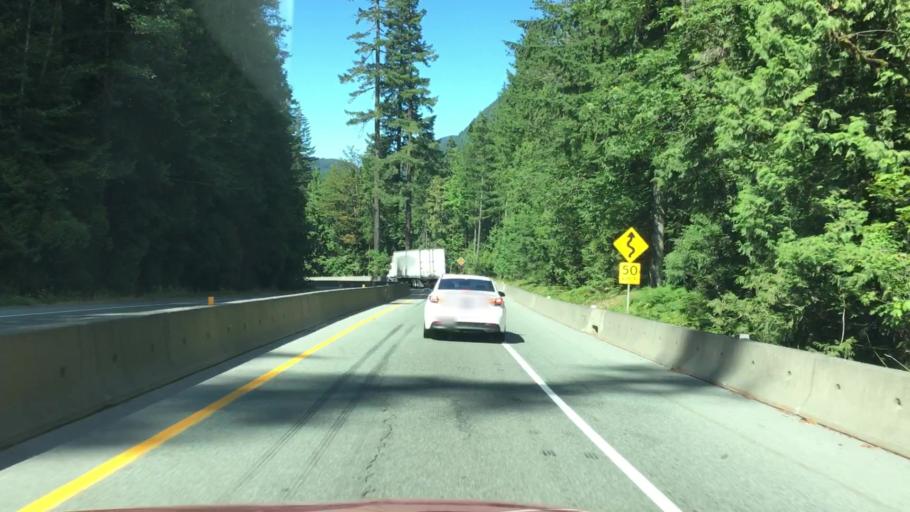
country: CA
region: British Columbia
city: Port Alberni
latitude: 49.2500
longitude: -124.6603
